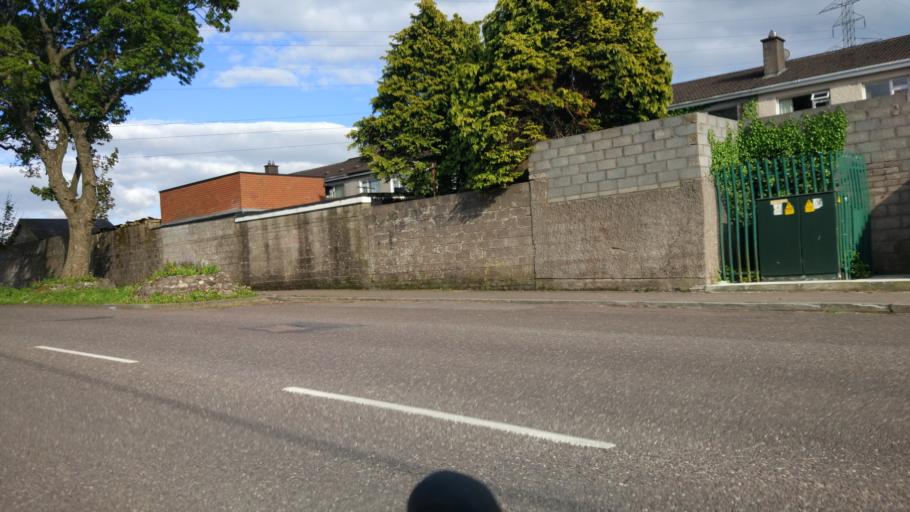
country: IE
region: Munster
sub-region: County Cork
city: Cork
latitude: 51.9115
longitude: -8.4423
